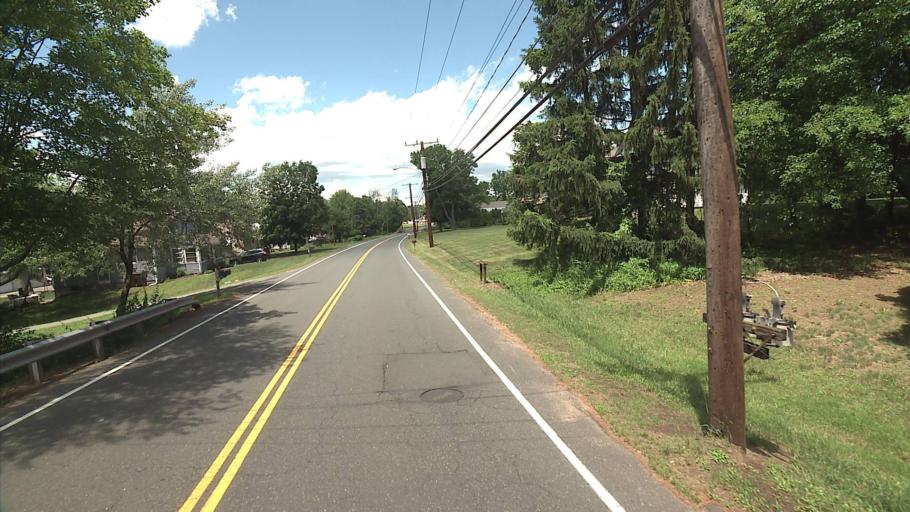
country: US
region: Connecticut
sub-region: Hartford County
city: Hazardville
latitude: 42.0064
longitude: -72.5425
